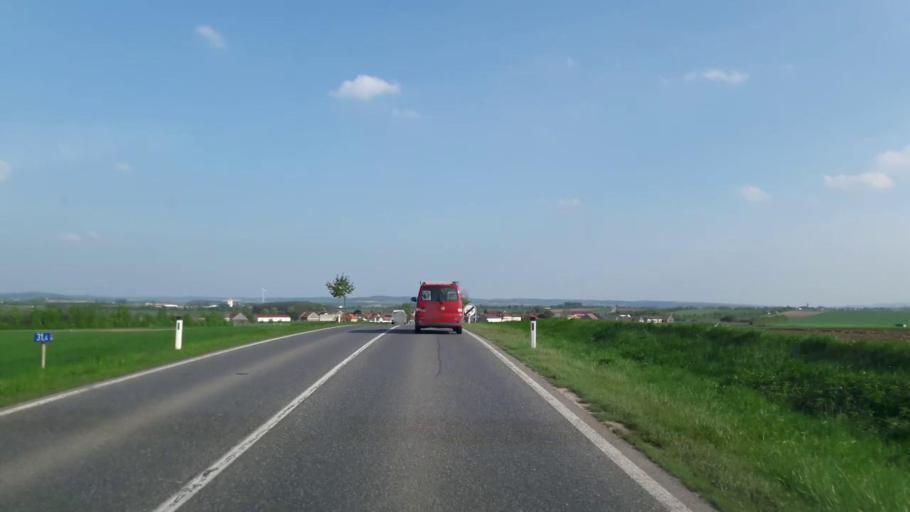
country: AT
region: Lower Austria
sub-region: Politischer Bezirk Hollabrunn
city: Guntersdorf
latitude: 48.6367
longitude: 16.0570
